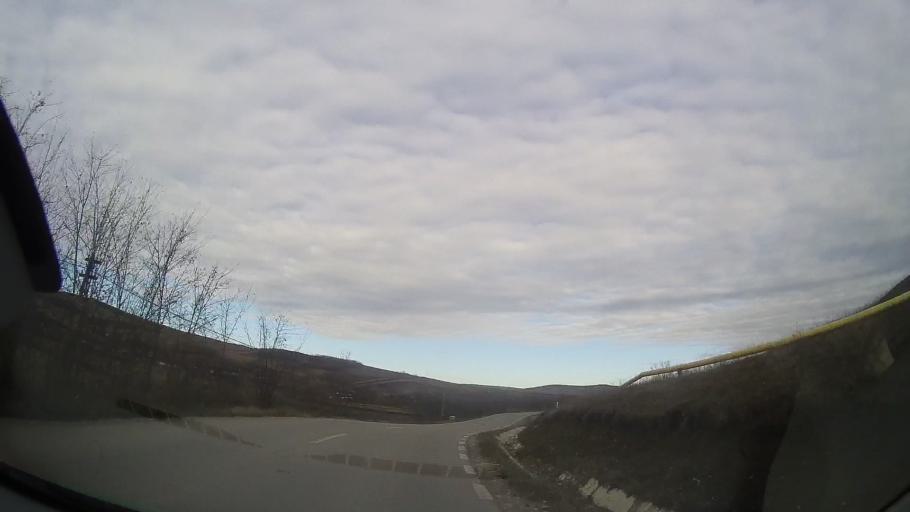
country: RO
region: Cluj
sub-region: Comuna Geaca
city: Geaca
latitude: 46.8441
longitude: 24.1370
